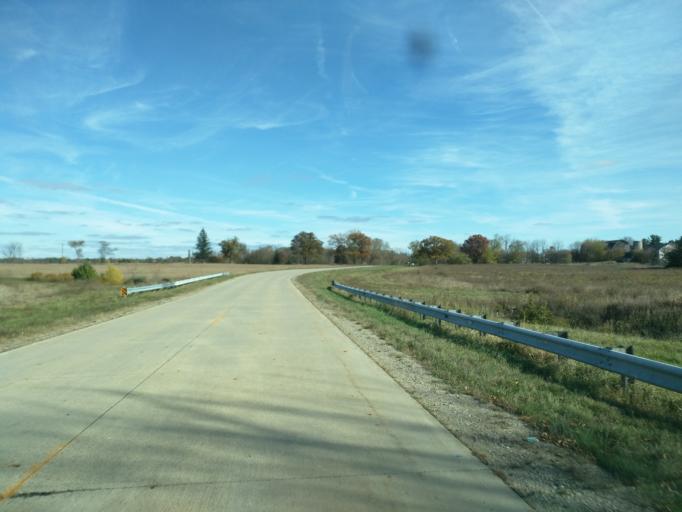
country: US
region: Michigan
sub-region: Ingham County
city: Edgemont Park
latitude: 42.7729
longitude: -84.5724
